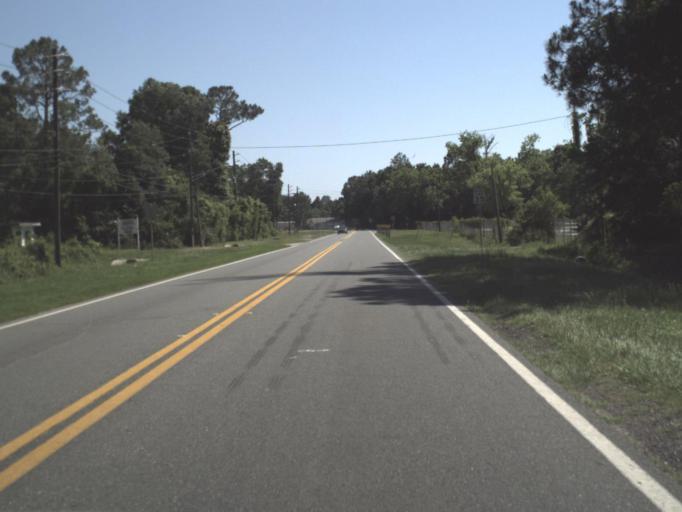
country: US
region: Florida
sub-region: Duval County
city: Baldwin
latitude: 30.3078
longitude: -81.9714
